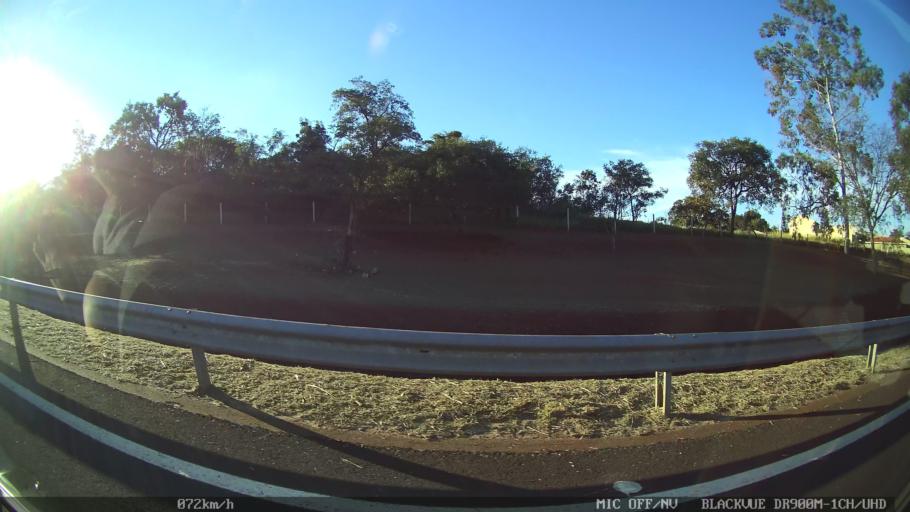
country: BR
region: Sao Paulo
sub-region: Araraquara
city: Araraquara
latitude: -21.8169
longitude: -48.1948
